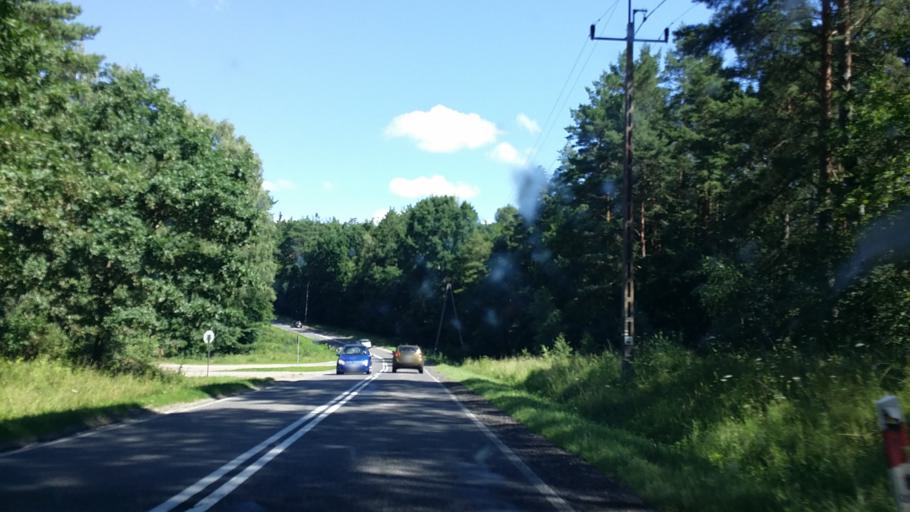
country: PL
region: West Pomeranian Voivodeship
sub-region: Powiat drawski
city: Drawsko Pomorskie
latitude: 53.4587
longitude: 15.8263
